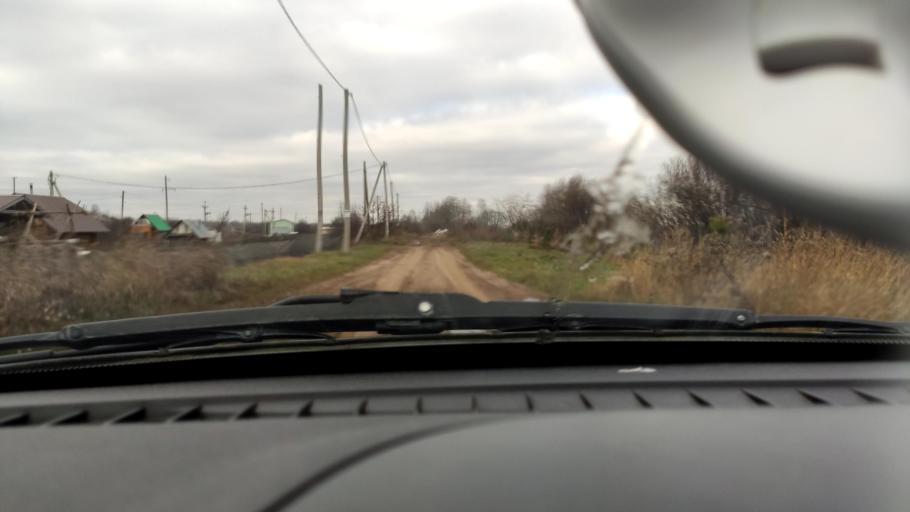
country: RU
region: Perm
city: Kondratovo
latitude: 57.9902
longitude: 56.0753
